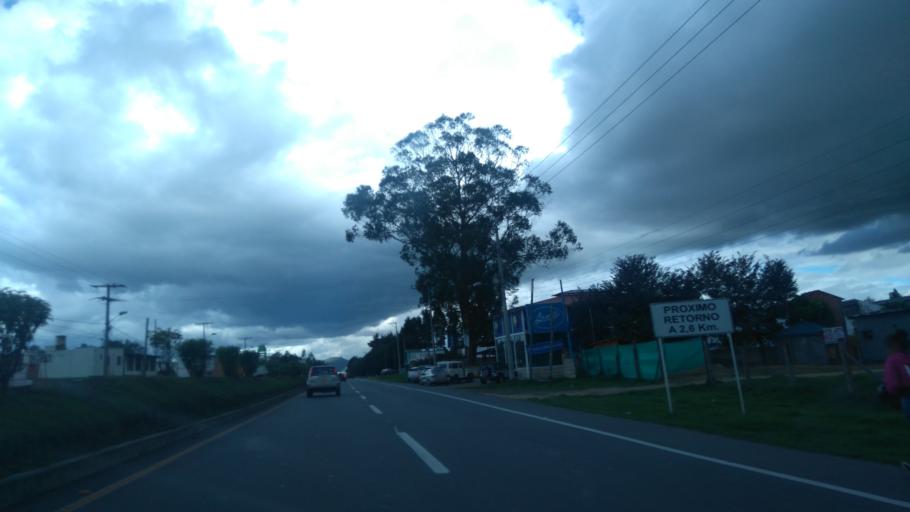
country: CO
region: Cundinamarca
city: El Rosal
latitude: 4.8345
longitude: -74.2506
